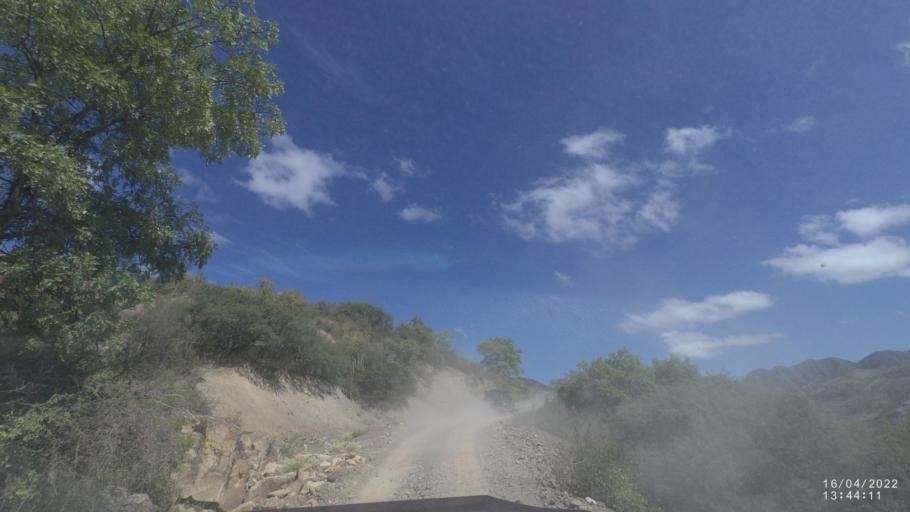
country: BO
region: Cochabamba
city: Mizque
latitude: -17.9973
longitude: -65.5916
